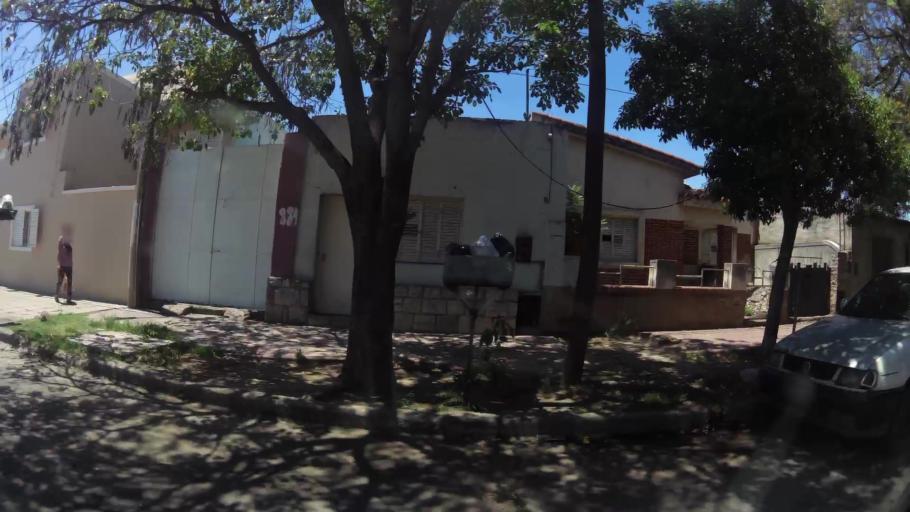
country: AR
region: Cordoba
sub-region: Departamento de Capital
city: Cordoba
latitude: -31.3975
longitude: -64.2120
